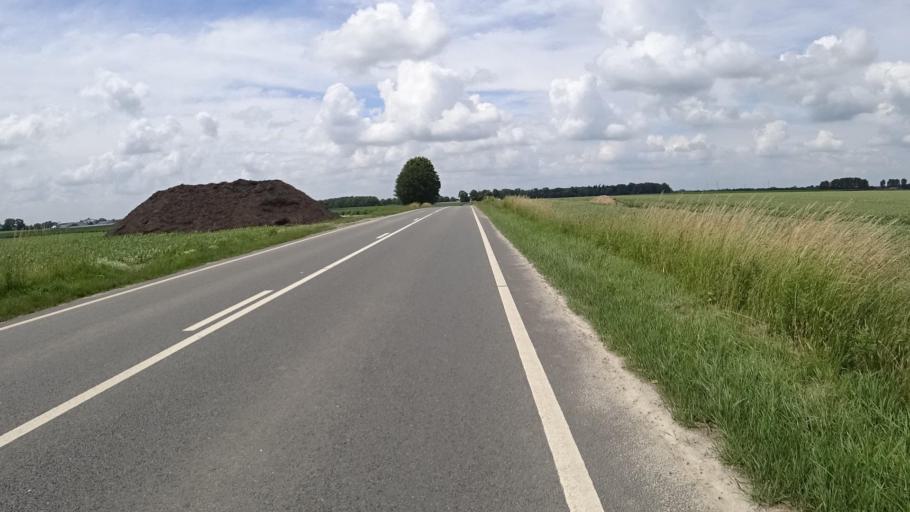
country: BE
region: Wallonia
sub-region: Province du Brabant Wallon
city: Perwez
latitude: 50.5469
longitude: 4.8344
